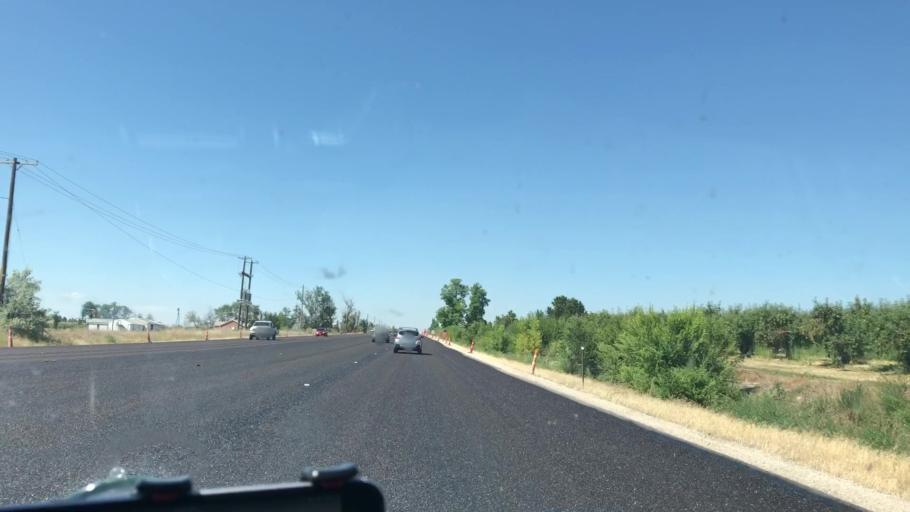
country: US
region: Idaho
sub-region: Owyhee County
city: Marsing
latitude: 43.5888
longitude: -116.7922
